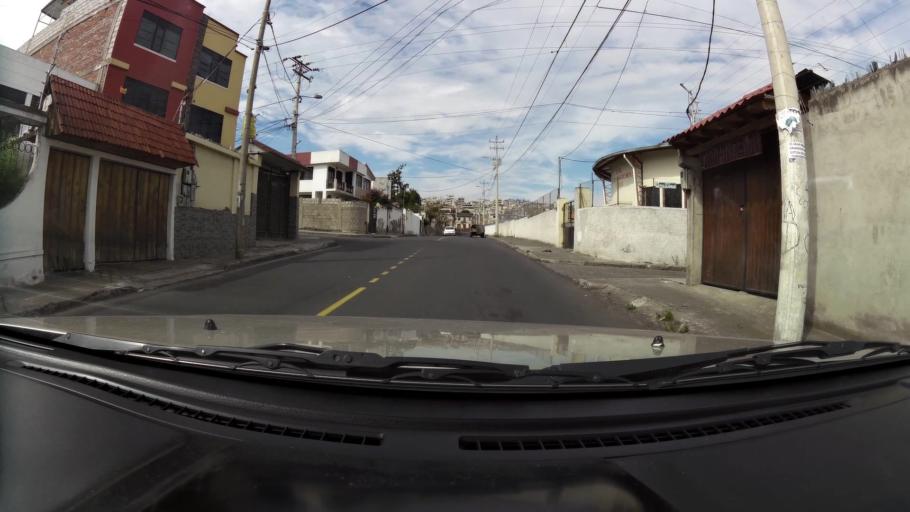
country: EC
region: Tungurahua
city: Ambato
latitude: -1.2470
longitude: -78.6194
